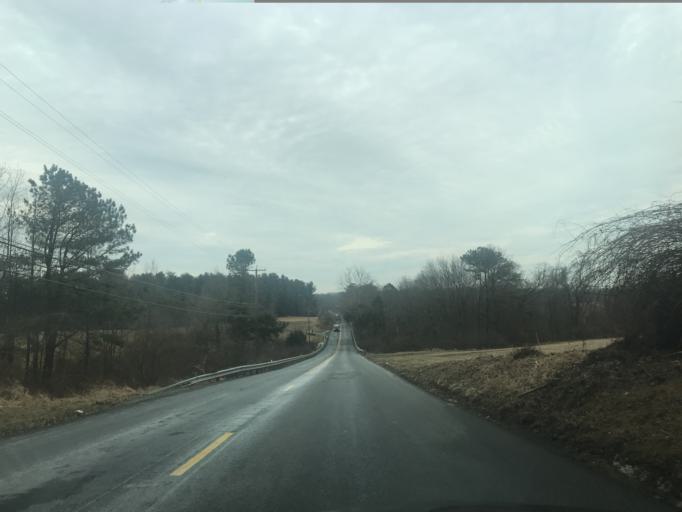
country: US
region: Maryland
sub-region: Harford County
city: Jarrettsville
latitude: 39.6997
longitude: -76.4759
